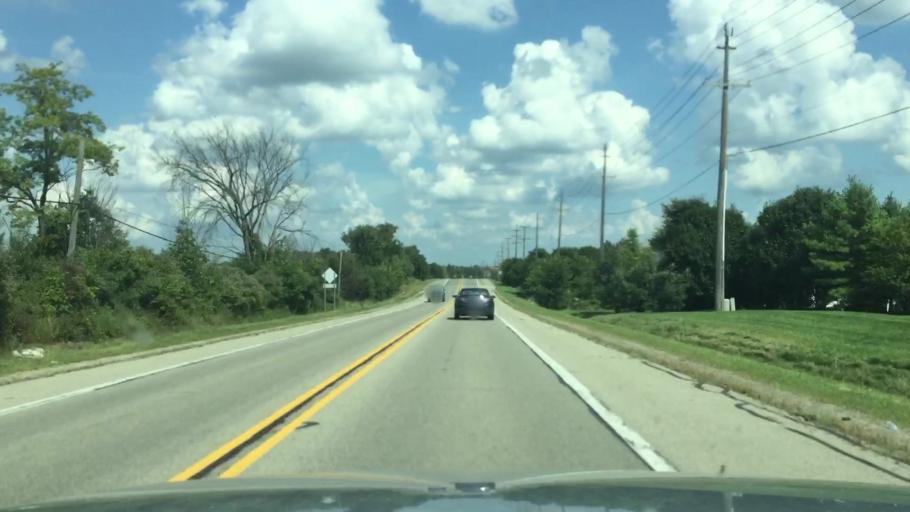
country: US
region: Michigan
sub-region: Washtenaw County
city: Saline
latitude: 42.1572
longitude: -83.8045
